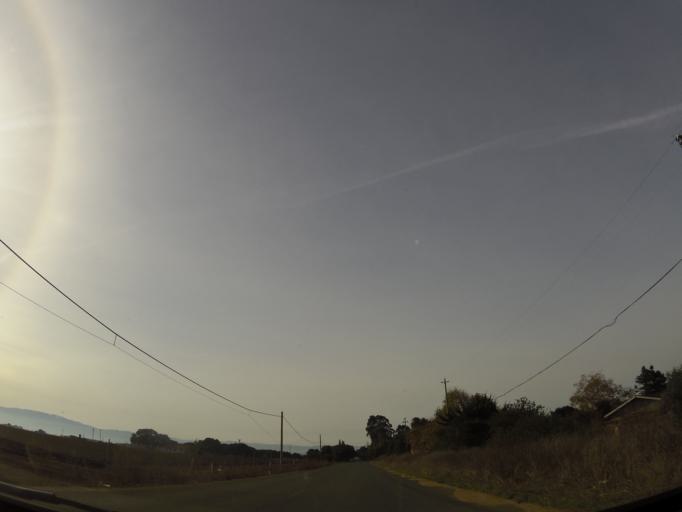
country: US
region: California
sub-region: Monterey County
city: Prunedale
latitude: 36.7470
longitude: -121.6266
